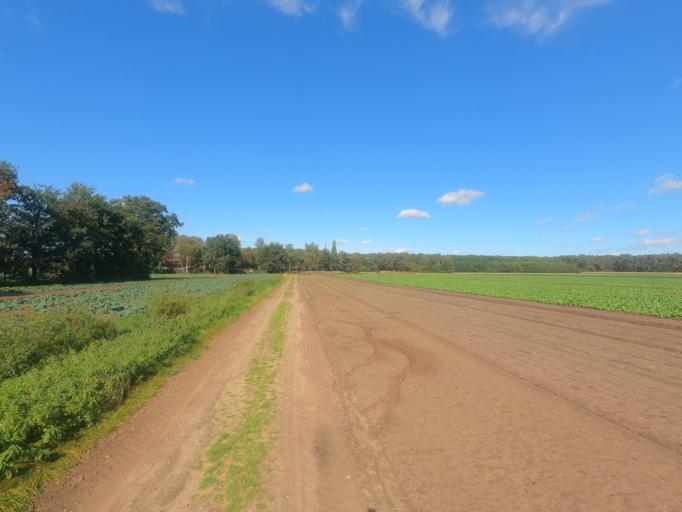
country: BE
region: Flanders
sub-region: Provincie Antwerpen
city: Lille
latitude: 51.2117
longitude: 4.8341
